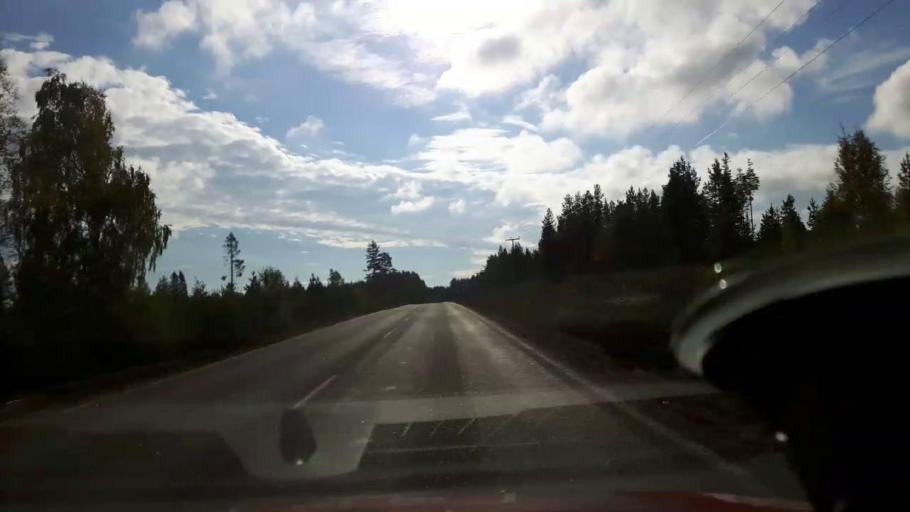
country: SE
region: Vaesternorrland
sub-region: Ange Kommun
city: Ange
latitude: 62.0956
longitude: 15.0823
